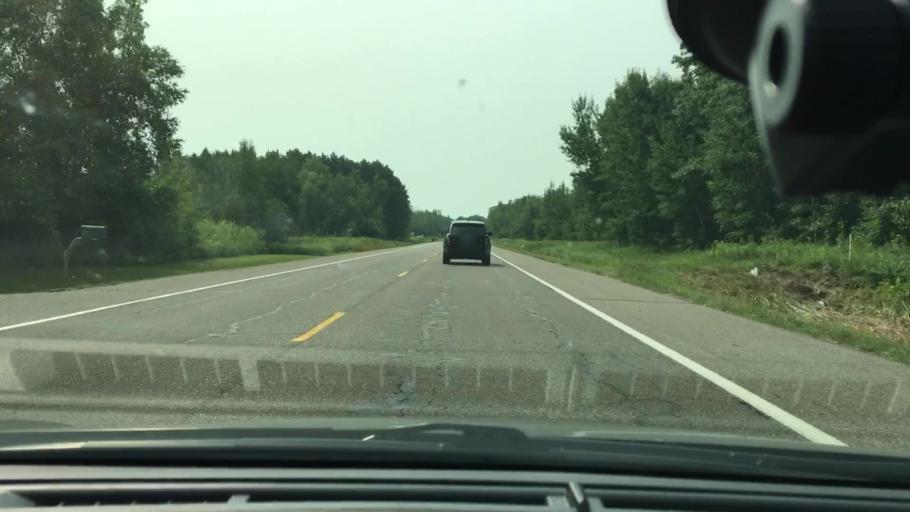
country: US
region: Minnesota
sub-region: Crow Wing County
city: Brainerd
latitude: 46.3912
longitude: -94.2233
